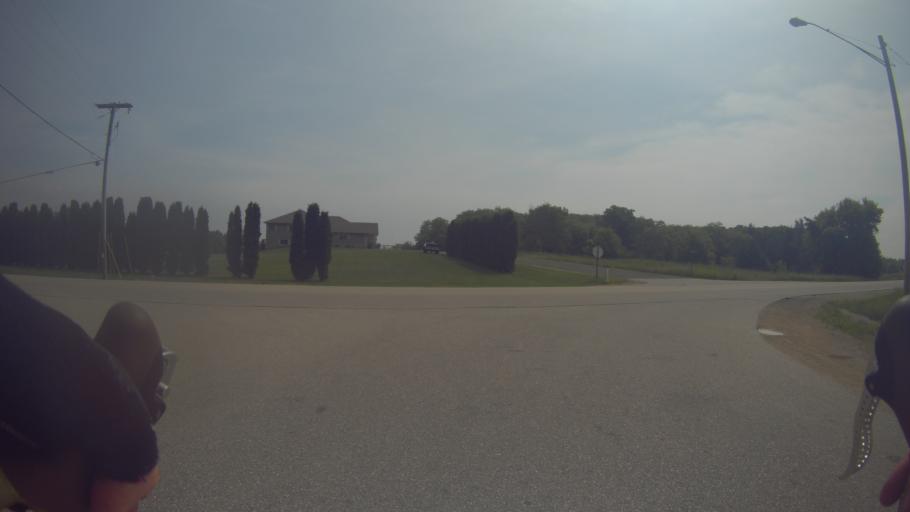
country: US
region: Wisconsin
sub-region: Rock County
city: Edgerton
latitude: 42.8550
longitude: -89.0267
